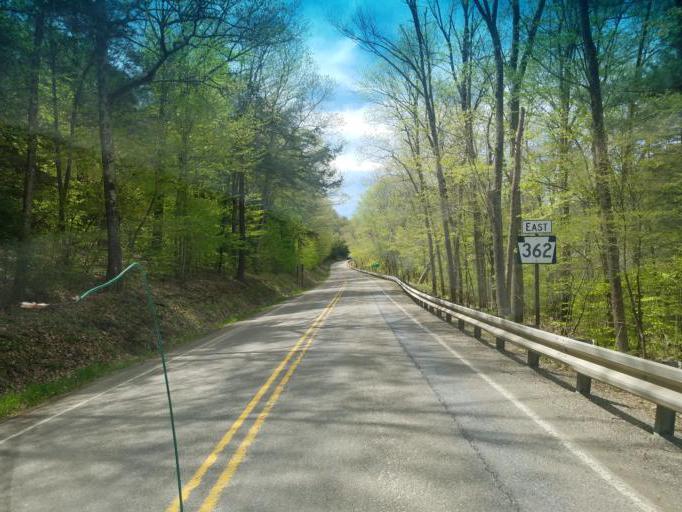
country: US
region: Pennsylvania
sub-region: Tioga County
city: Wellsboro
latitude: 41.7459
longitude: -77.4261
